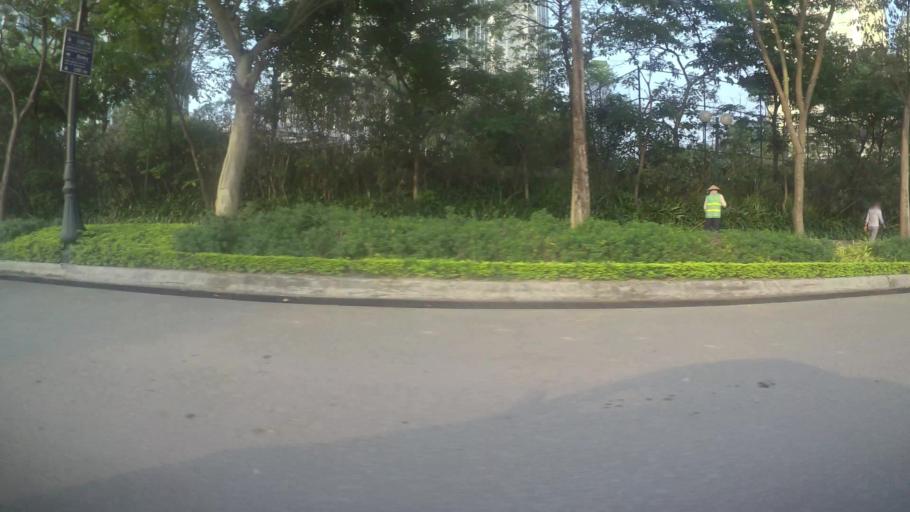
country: VN
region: Ha Noi
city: Tay Ho
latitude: 21.0794
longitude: 105.7915
